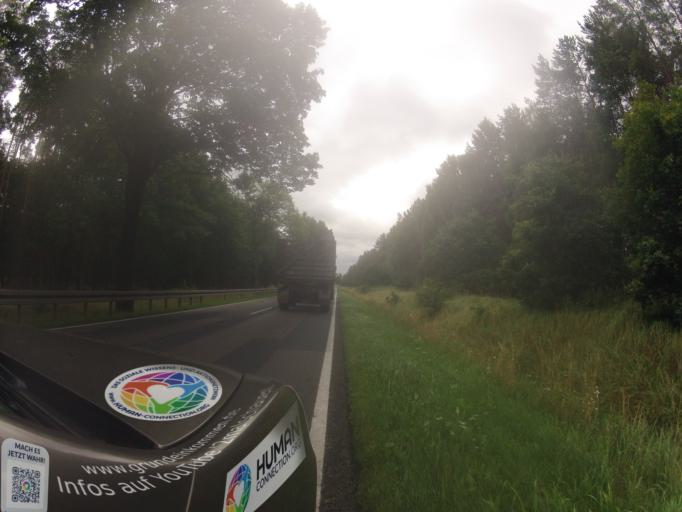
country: DE
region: Mecklenburg-Vorpommern
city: Jatznick
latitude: 53.6248
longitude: 13.9302
